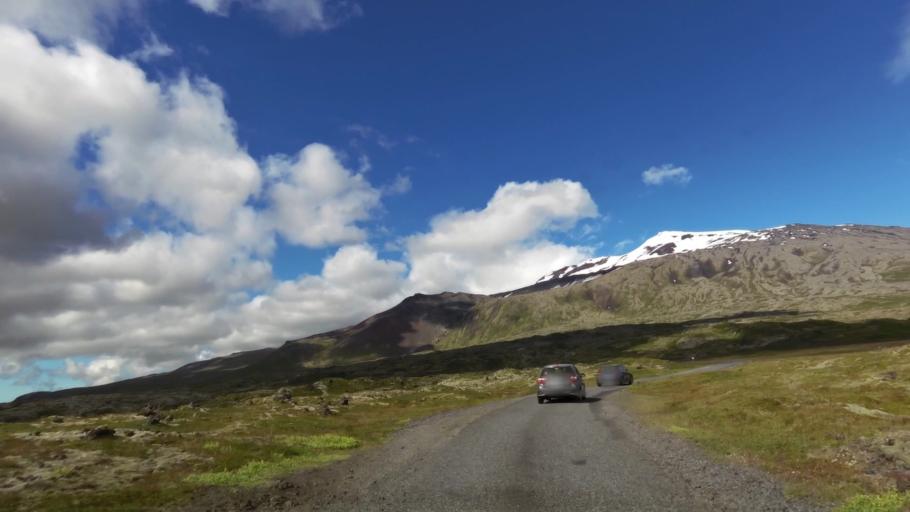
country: IS
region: West
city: Olafsvik
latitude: 64.7649
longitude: -23.8767
